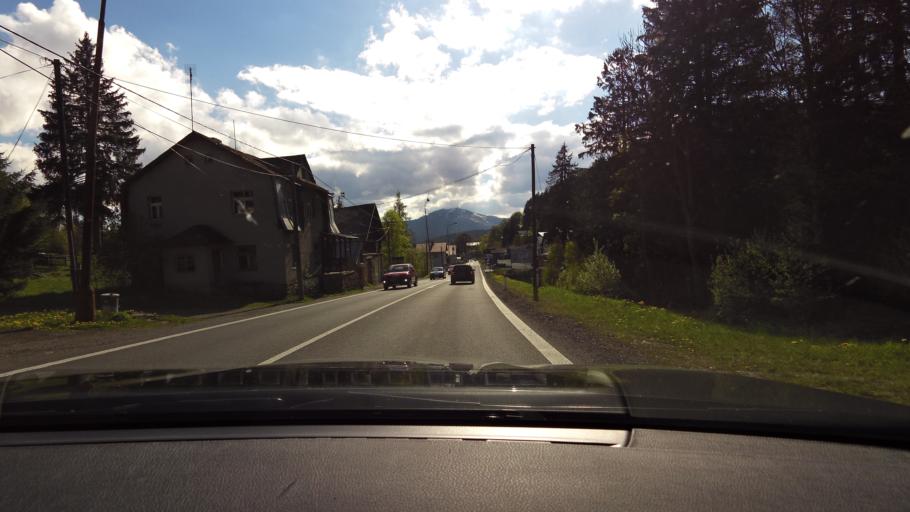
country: CZ
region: Plzensky
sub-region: Okres Klatovy
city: Zelezna Ruda
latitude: 49.1400
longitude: 13.2434
